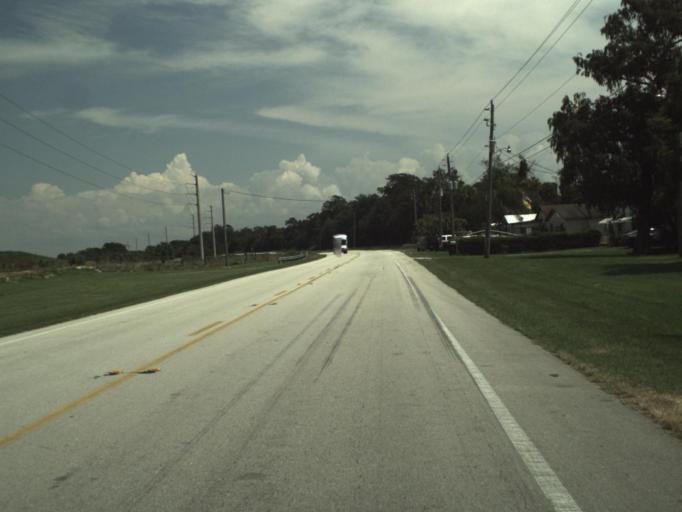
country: US
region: Florida
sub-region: Palm Beach County
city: Pahokee
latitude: 26.8987
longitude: -80.6114
